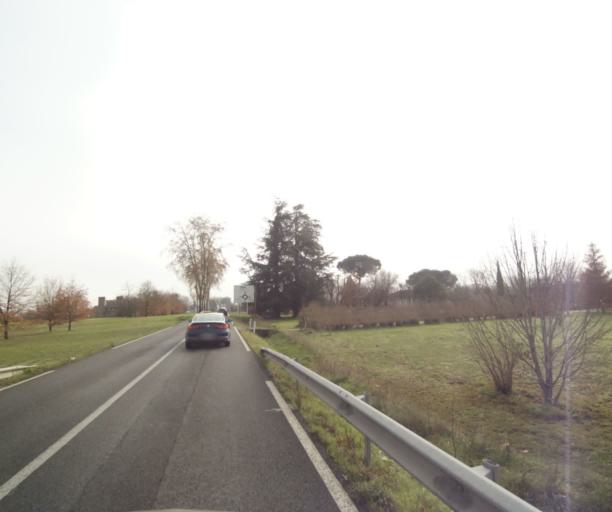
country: FR
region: Midi-Pyrenees
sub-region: Departement de la Haute-Garonne
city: Villemur-sur-Tarn
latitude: 43.8485
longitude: 1.4914
